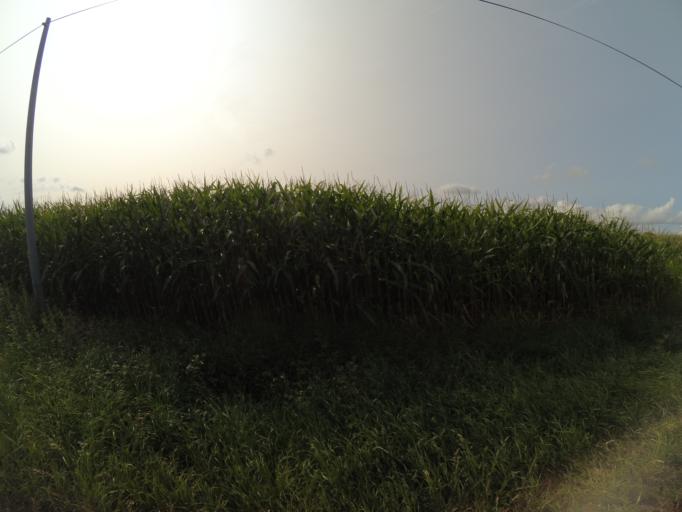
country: FR
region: Pays de la Loire
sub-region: Departement de la Vendee
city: Bouffere
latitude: 46.9391
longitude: -1.3309
